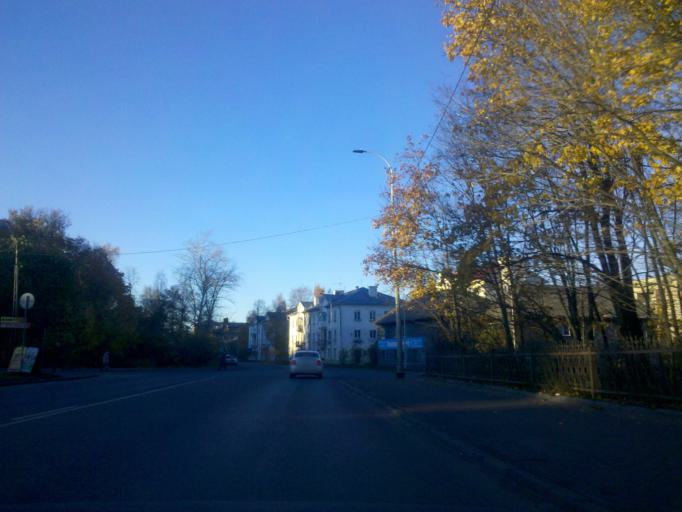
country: RU
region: Republic of Karelia
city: Petrozavodsk
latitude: 61.7799
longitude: 34.3887
